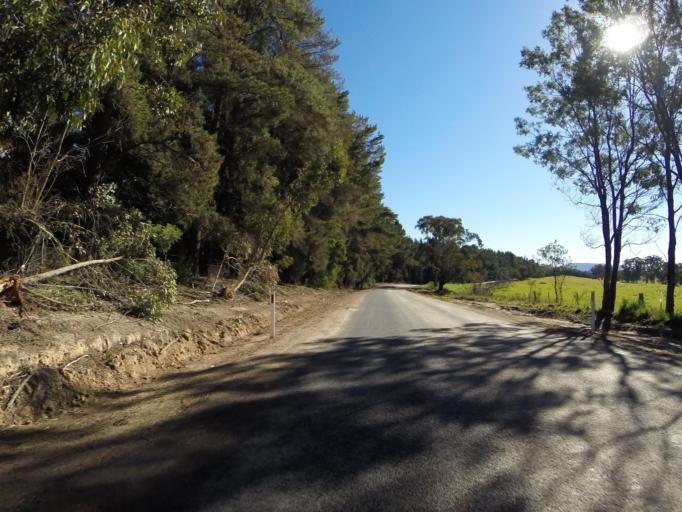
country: AU
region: New South Wales
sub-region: Oberon
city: Oberon
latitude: -33.6037
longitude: 149.8454
